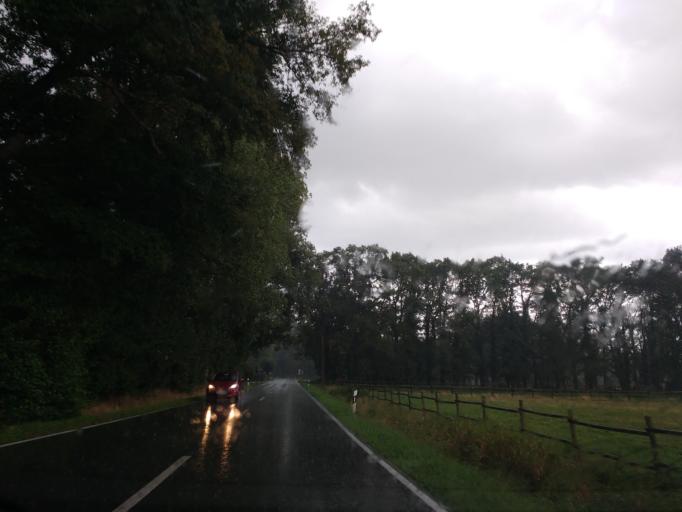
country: DE
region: North Rhine-Westphalia
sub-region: Regierungsbezirk Munster
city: Lienen
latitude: 52.1140
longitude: 7.9355
